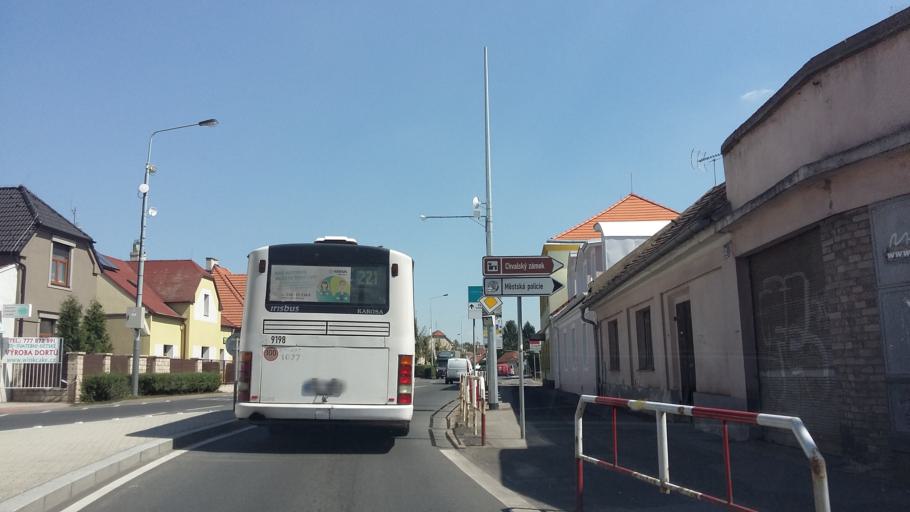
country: CZ
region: Praha
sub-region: Praha 20
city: Horni Pocernice
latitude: 50.1124
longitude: 14.5946
